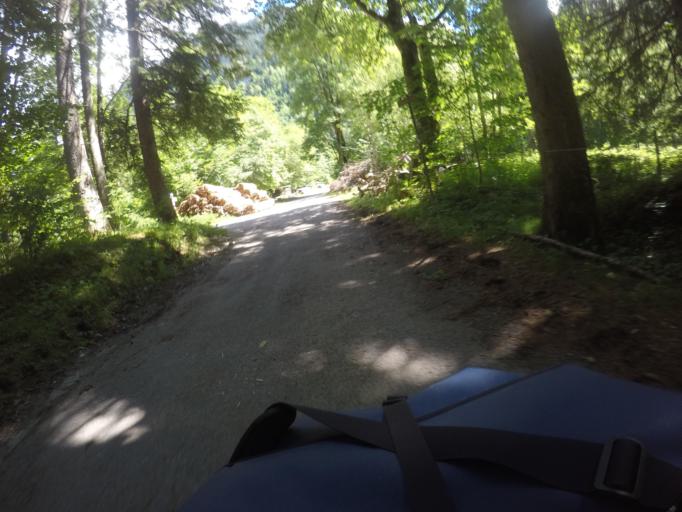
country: DE
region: Bavaria
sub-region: Swabia
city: Schwangau
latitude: 47.5616
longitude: 10.7504
